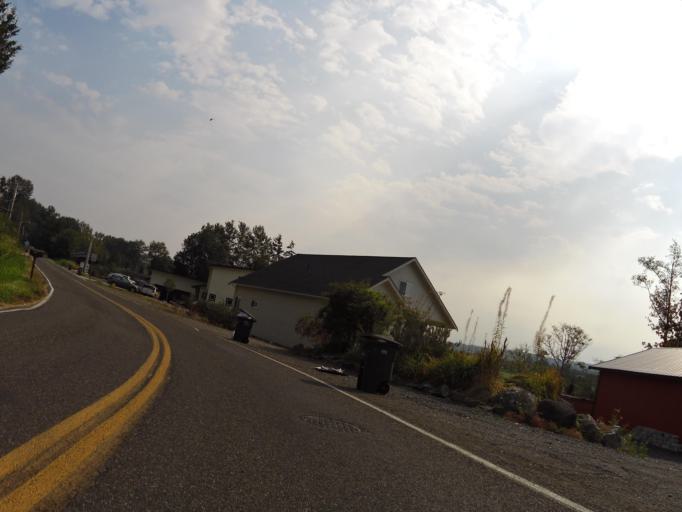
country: US
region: Washington
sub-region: Whatcom County
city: Ferndale
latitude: 48.8053
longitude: -122.6825
